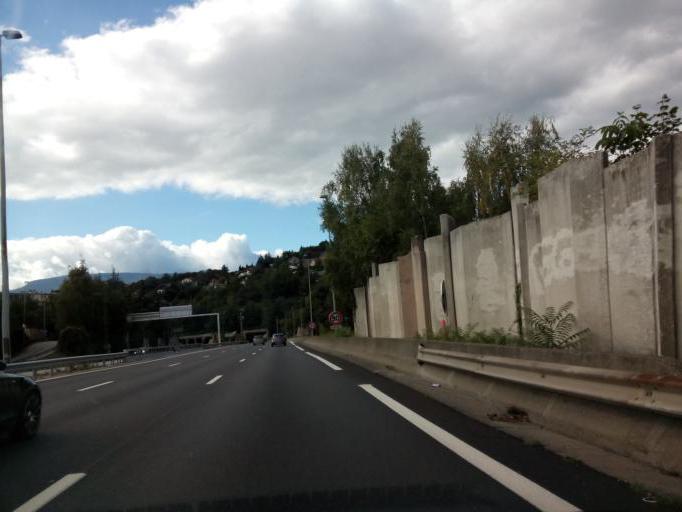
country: FR
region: Rhone-Alpes
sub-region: Departement de la Savoie
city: Chambery
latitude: 45.5715
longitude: 5.9369
